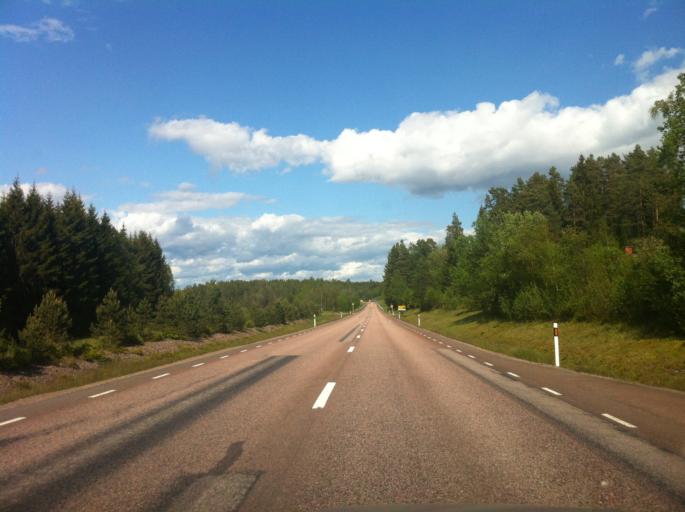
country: SE
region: Vaermland
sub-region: Kristinehamns Kommun
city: Kristinehamn
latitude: 59.3856
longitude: 14.1836
